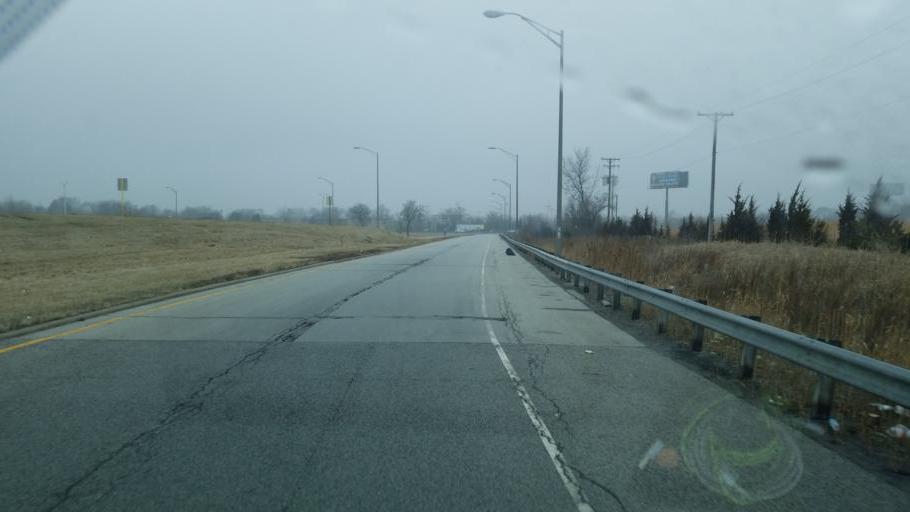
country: US
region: Illinois
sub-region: Cook County
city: South Holland
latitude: 41.6014
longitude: -87.5809
